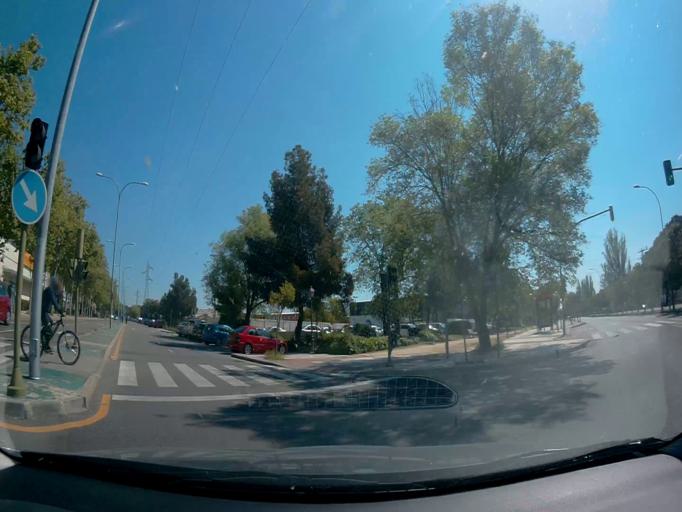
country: ES
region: Madrid
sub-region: Provincia de Madrid
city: Alcorcon
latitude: 40.3440
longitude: -3.8085
